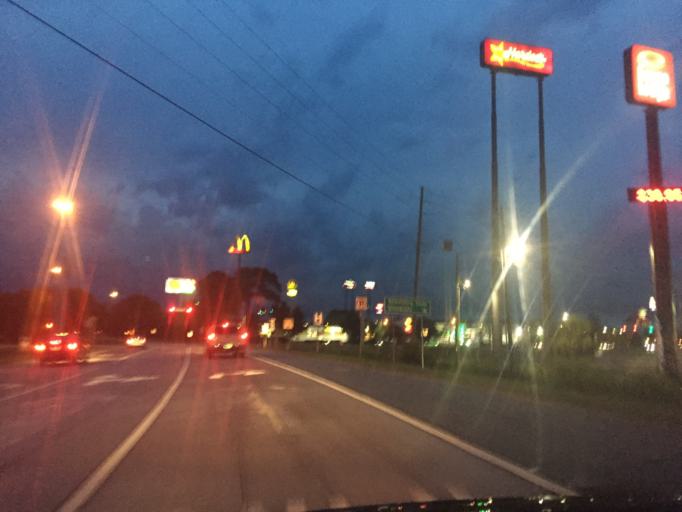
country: US
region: Georgia
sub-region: Chatham County
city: Georgetown
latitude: 32.0036
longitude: -81.2831
